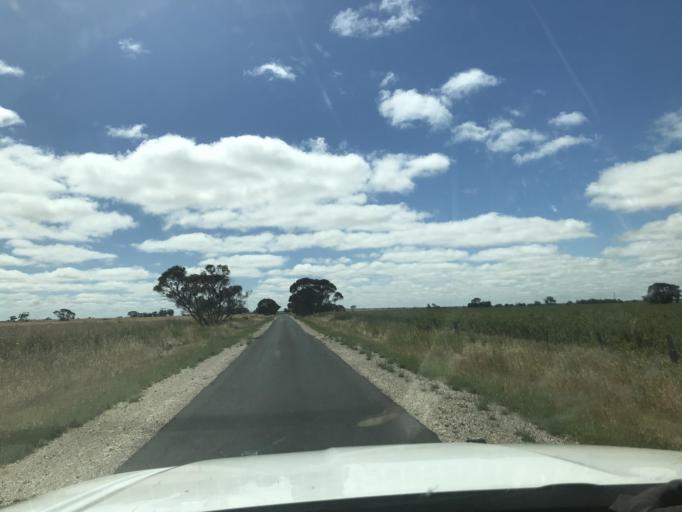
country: AU
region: South Australia
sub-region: Tatiara
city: Bordertown
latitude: -36.2815
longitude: 141.1422
